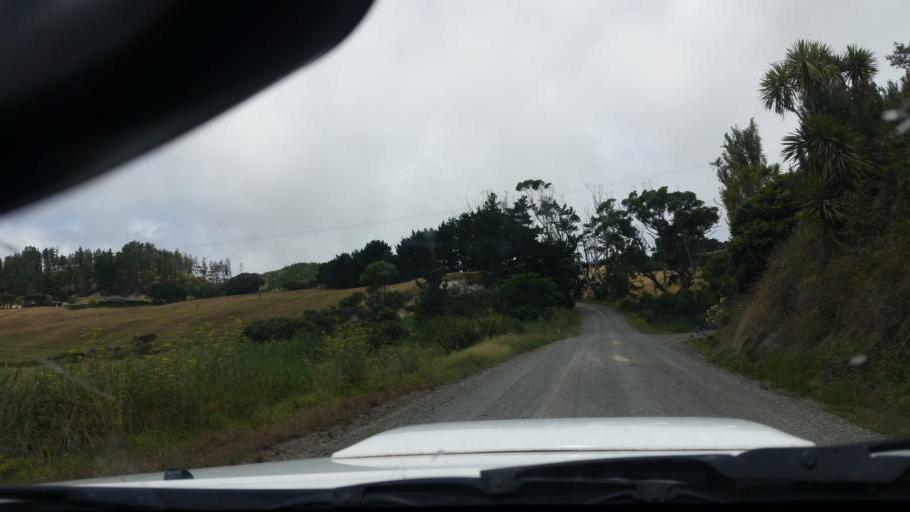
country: NZ
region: Northland
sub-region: Kaipara District
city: Dargaville
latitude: -35.8365
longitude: 173.6608
